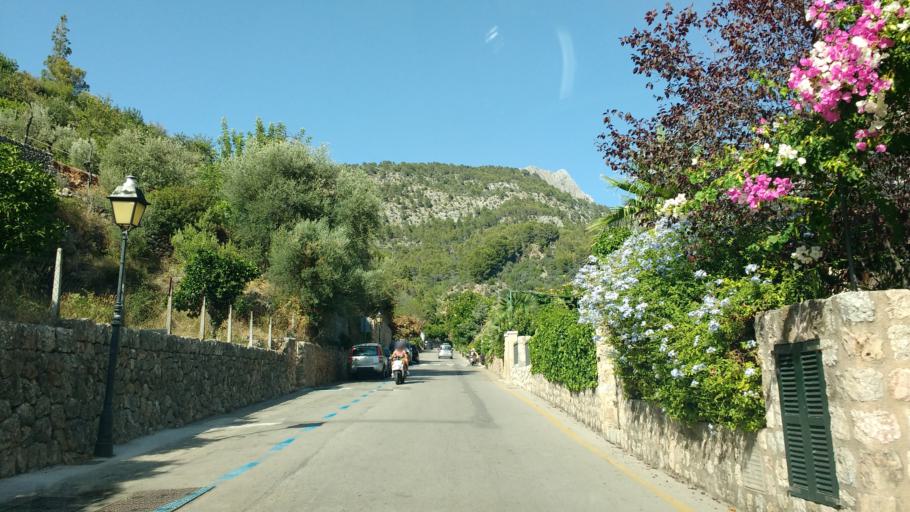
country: ES
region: Balearic Islands
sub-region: Illes Balears
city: Fornalutx
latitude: 39.7835
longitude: 2.7423
